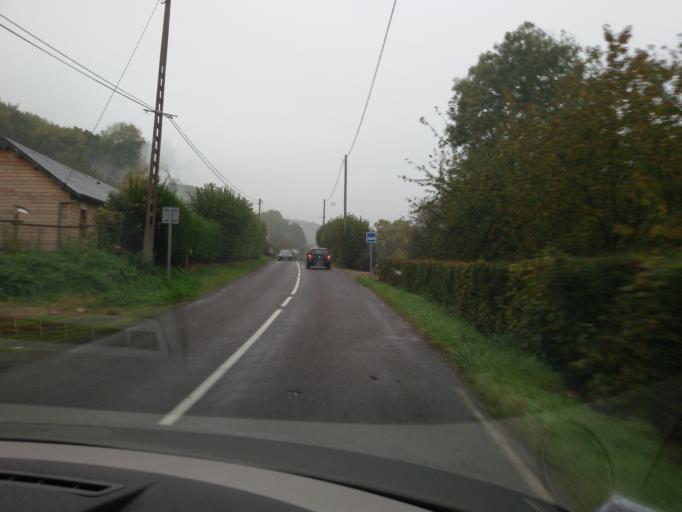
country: FR
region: Lower Normandy
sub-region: Departement du Calvados
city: Ablon
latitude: 49.4201
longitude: 0.3176
